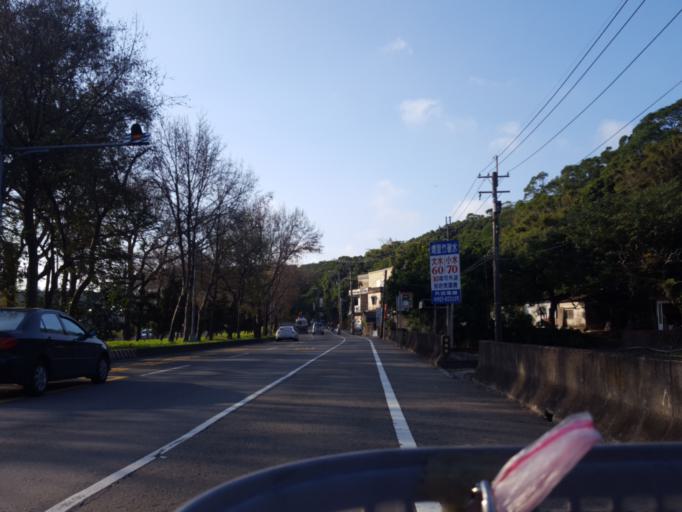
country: TW
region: Taiwan
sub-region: Hsinchu
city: Zhubei
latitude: 24.8576
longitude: 120.9990
